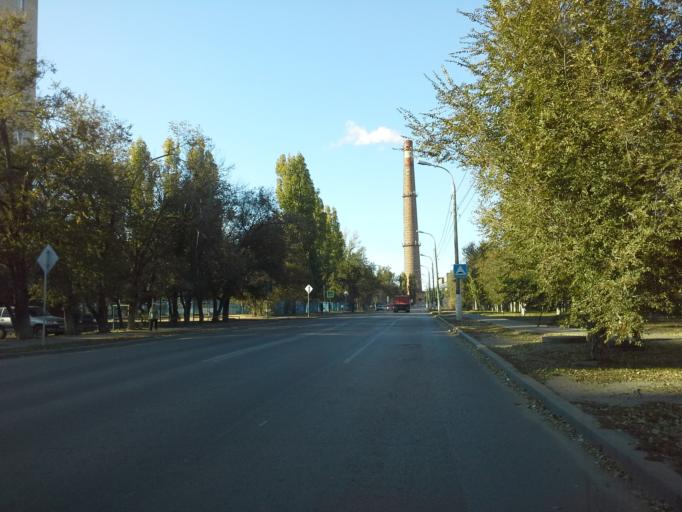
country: RU
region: Volgograd
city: Vodstroy
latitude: 48.8229
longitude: 44.6302
